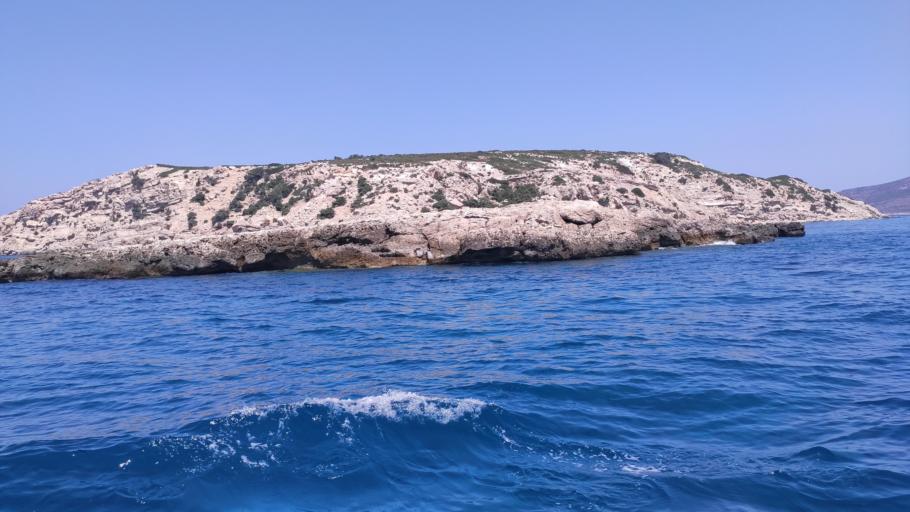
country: GR
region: South Aegean
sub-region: Nomos Dodekanisou
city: Pylion
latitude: 36.9323
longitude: 27.0946
